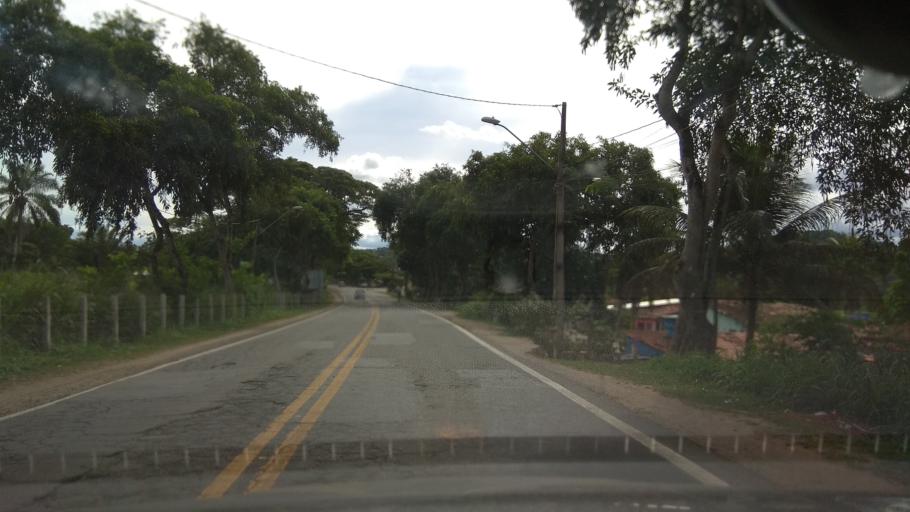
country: BR
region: Bahia
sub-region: Ubata
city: Ubata
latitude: -14.2005
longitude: -39.5342
